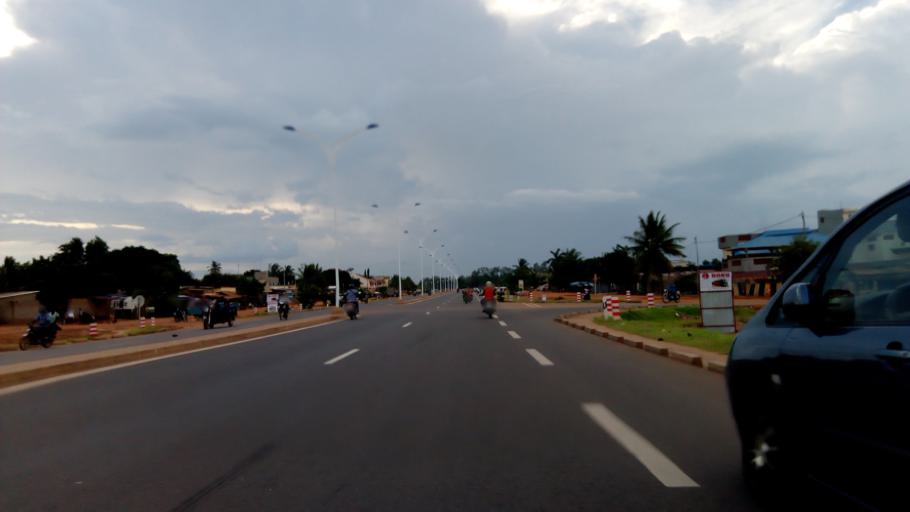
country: TG
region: Maritime
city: Lome
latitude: 6.2433
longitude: 1.1961
